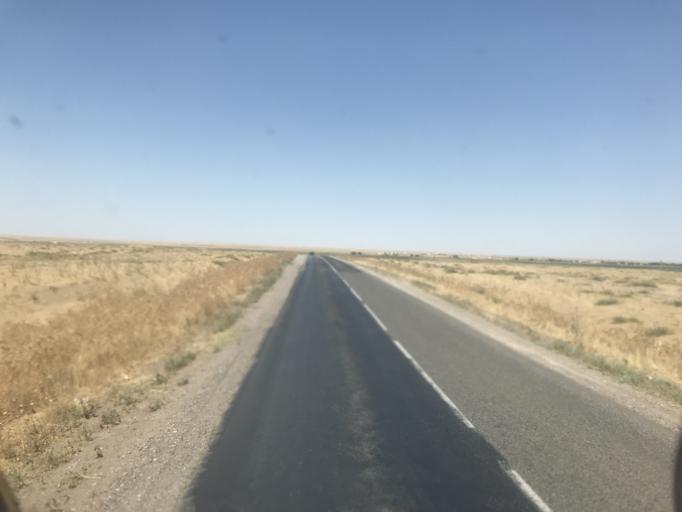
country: UZ
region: Toshkent
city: Chinoz
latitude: 41.1917
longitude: 68.6214
